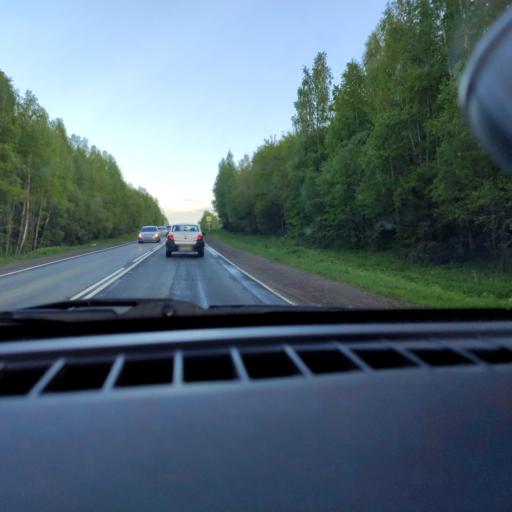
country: RU
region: Perm
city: Perm
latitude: 58.1481
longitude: 56.2598
